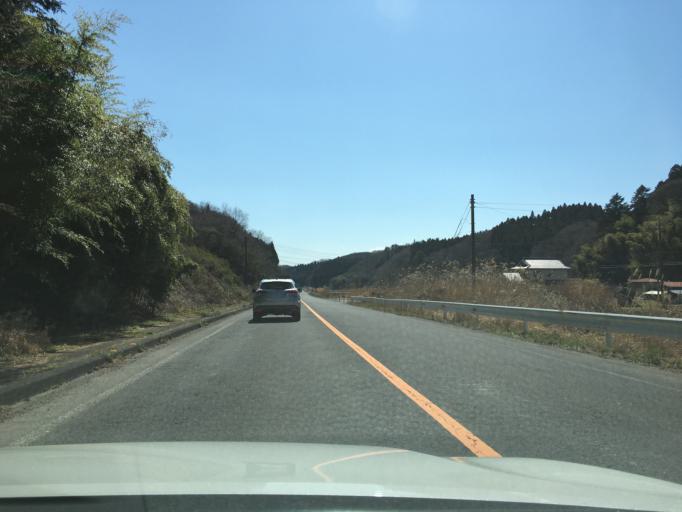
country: JP
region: Tochigi
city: Kuroiso
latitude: 37.0490
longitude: 140.1706
